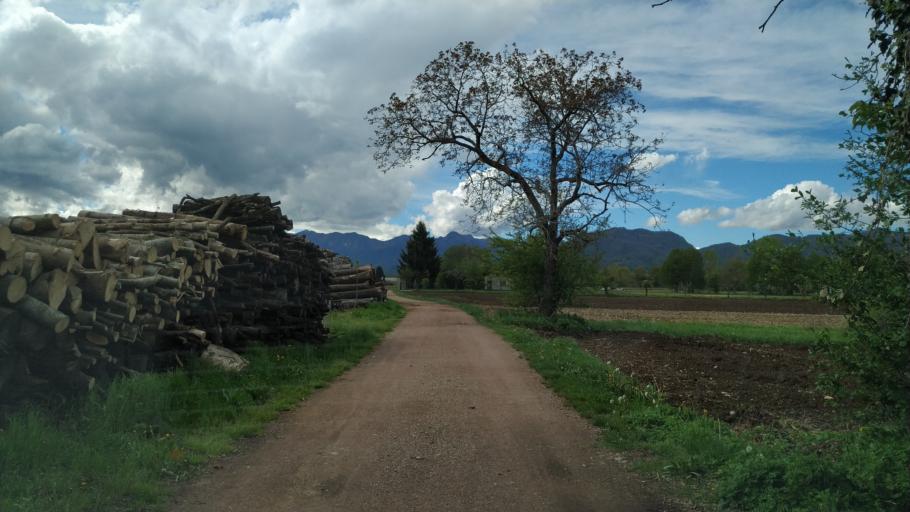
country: IT
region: Piedmont
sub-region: Provincia di Novara
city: Prato Sesia
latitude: 45.6554
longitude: 8.3673
